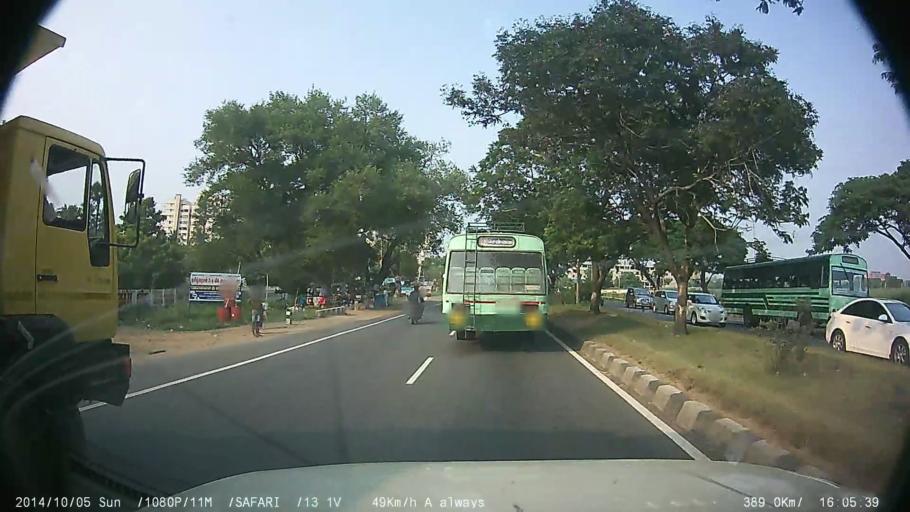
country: IN
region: Tamil Nadu
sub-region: Kancheepuram
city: Vandalur
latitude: 12.8707
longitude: 80.0768
